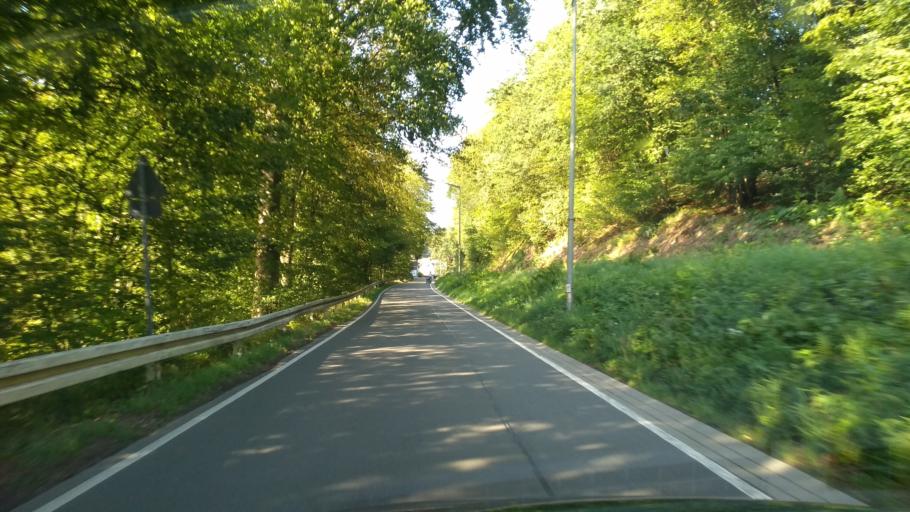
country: DE
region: North Rhine-Westphalia
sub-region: Regierungsbezirk Koln
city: Engelskirchen
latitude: 50.9901
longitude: 7.4597
